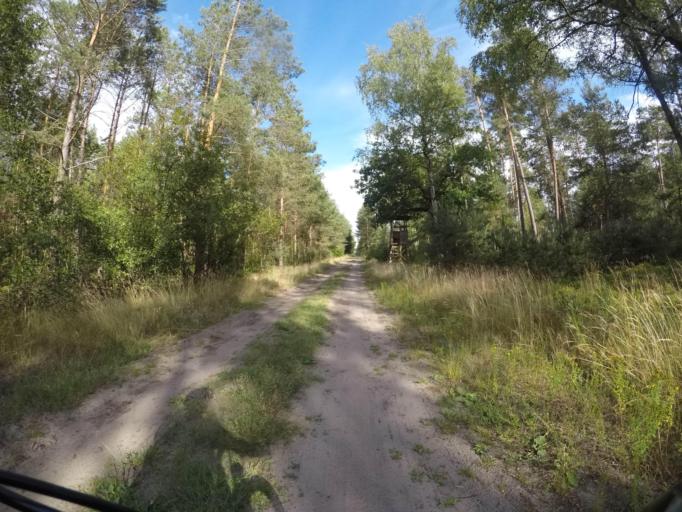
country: DE
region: Lower Saxony
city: Neu Darchau
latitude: 53.2744
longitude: 10.9631
